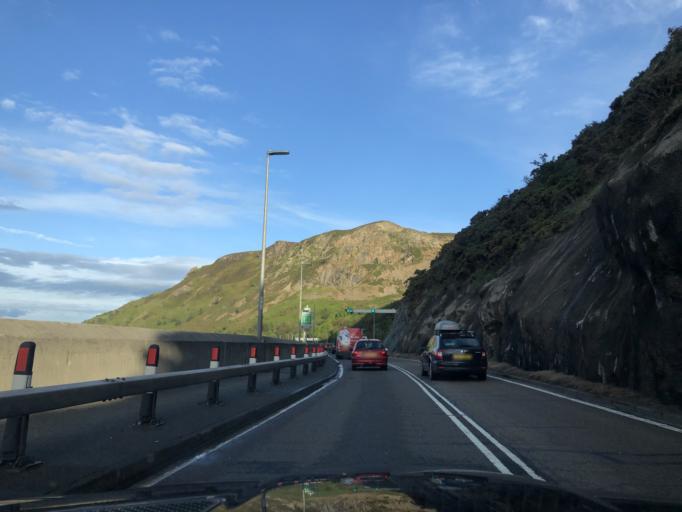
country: GB
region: Wales
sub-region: Conwy
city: Conwy
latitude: 53.2888
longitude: -3.8781
